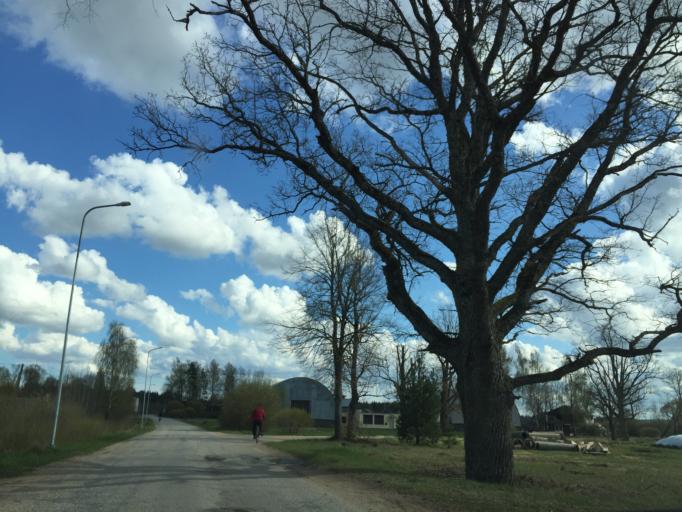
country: LV
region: Beverina
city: Murmuiza
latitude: 57.4697
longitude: 25.4959
